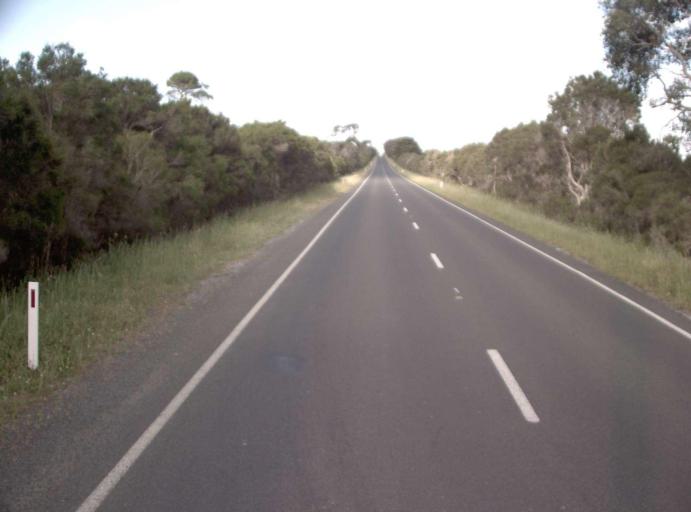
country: AU
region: Victoria
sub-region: Bass Coast
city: North Wonthaggi
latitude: -38.6027
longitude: 145.7713
